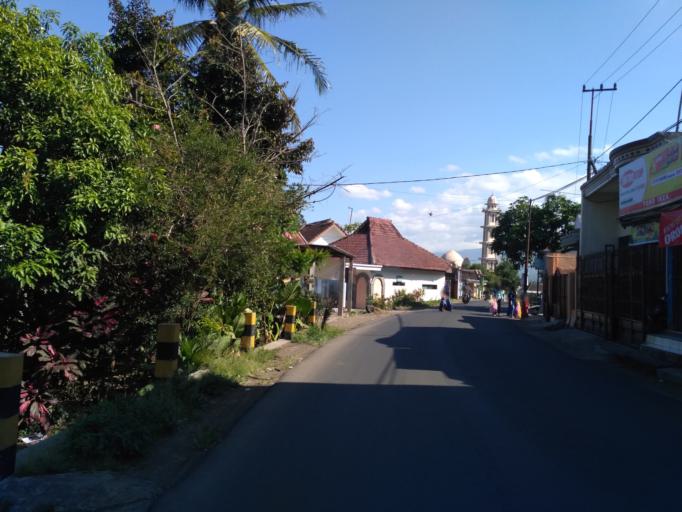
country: ID
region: East Java
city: Singosari
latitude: -7.9204
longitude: 112.6660
